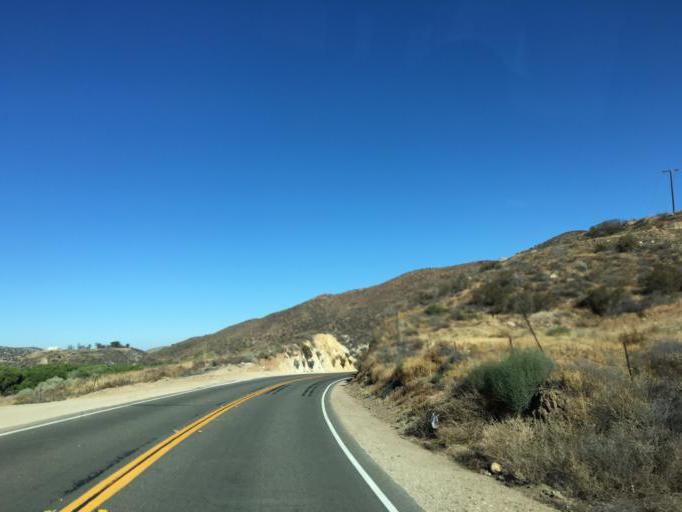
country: US
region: California
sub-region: Los Angeles County
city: Acton
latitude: 34.4378
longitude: -118.2369
